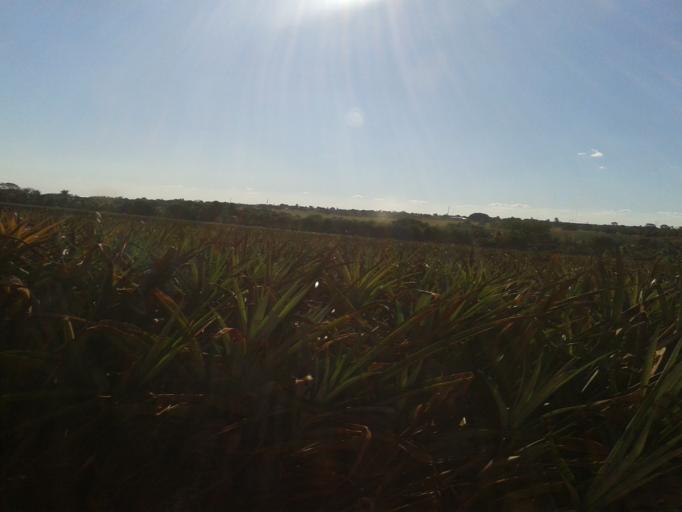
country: BR
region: Minas Gerais
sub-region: Centralina
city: Centralina
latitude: -18.7393
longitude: -49.1849
